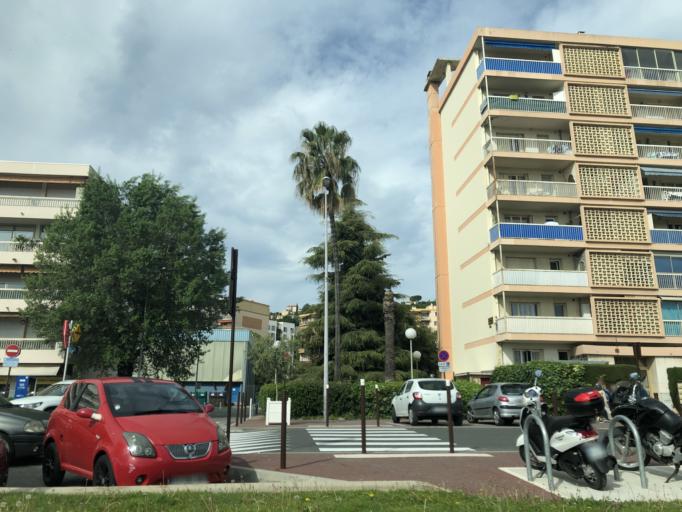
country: FR
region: Provence-Alpes-Cote d'Azur
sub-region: Departement des Alpes-Maritimes
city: Saint-Laurent-du-Var
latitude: 43.6787
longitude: 7.1908
